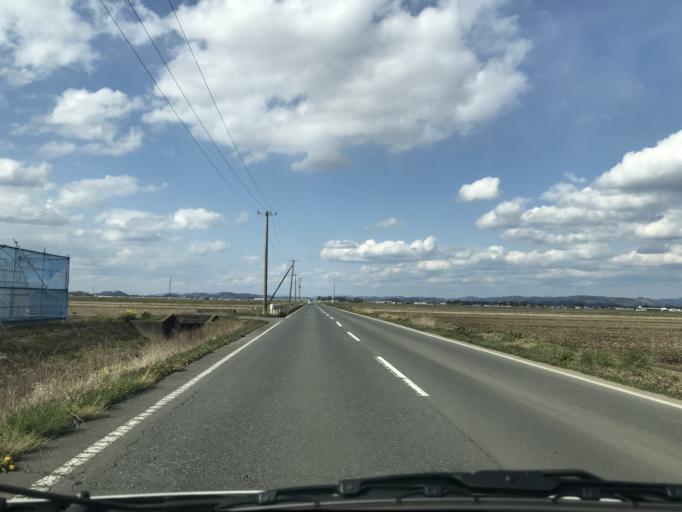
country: JP
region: Miyagi
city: Wakuya
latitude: 38.6639
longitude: 141.2303
